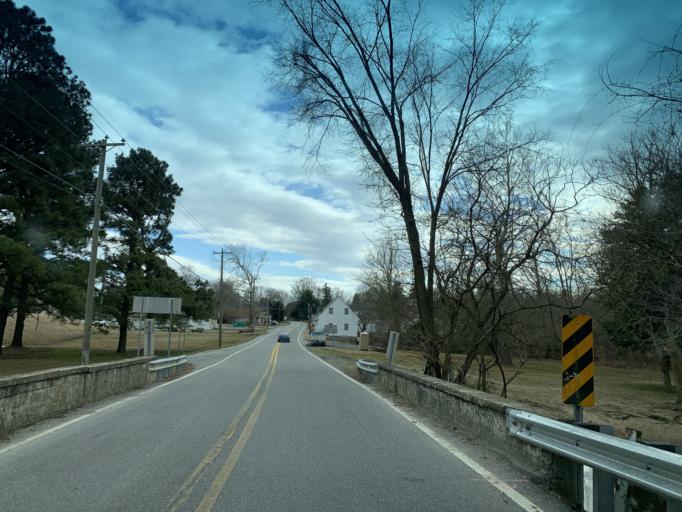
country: US
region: Maryland
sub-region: Queen Anne's County
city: Centreville
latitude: 38.9428
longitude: -76.0812
